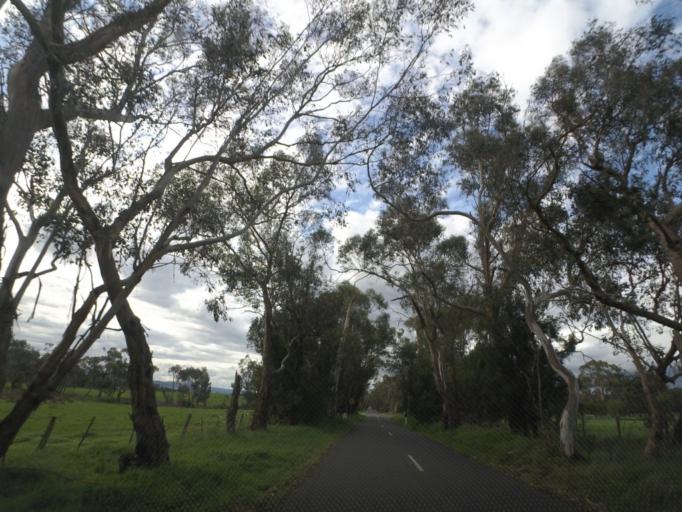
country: AU
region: Victoria
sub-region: Yarra Ranges
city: Mount Evelyn
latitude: -37.7402
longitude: 145.4131
